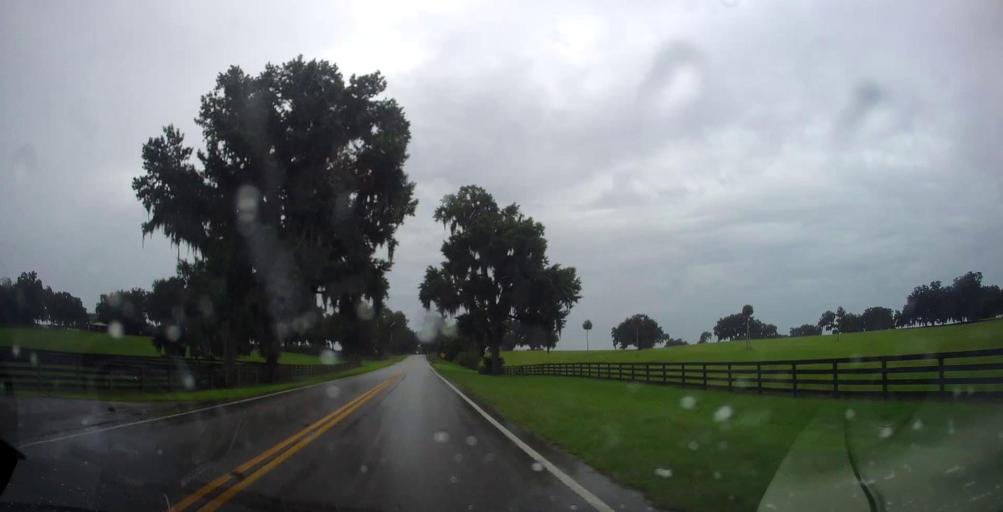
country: US
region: Florida
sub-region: Marion County
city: Citra
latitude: 29.3520
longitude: -82.2297
